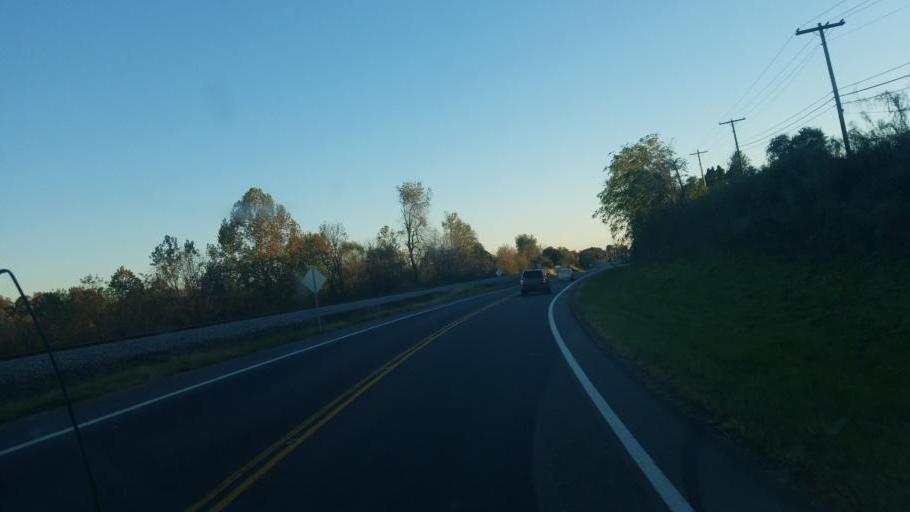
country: US
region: Ohio
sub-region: Licking County
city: Newark
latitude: 40.1194
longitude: -82.4284
